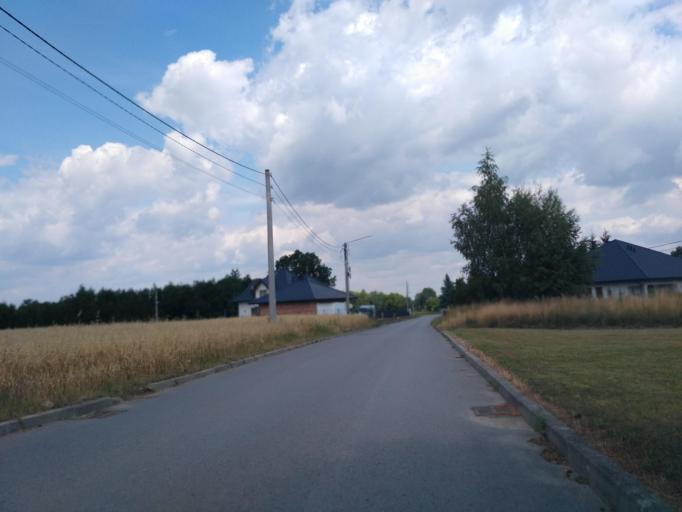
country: PL
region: Subcarpathian Voivodeship
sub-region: Powiat debicki
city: Pilzno
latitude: 49.9670
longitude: 21.2912
